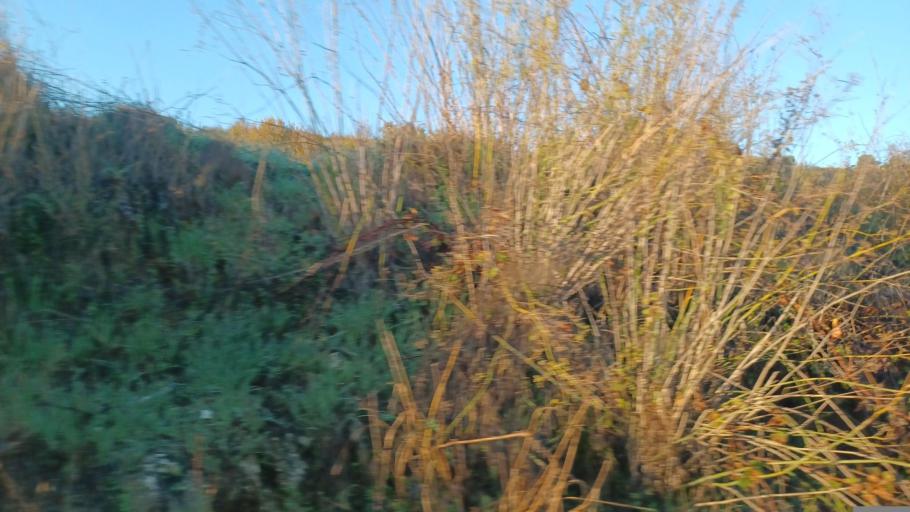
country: CY
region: Pafos
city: Mesogi
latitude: 34.8650
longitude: 32.5103
